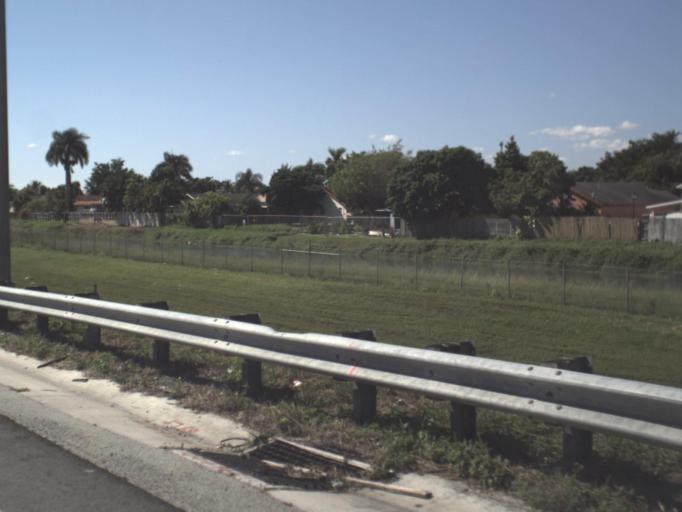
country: US
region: Florida
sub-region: Miami-Dade County
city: South Miami Heights
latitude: 25.6102
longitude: -80.3785
